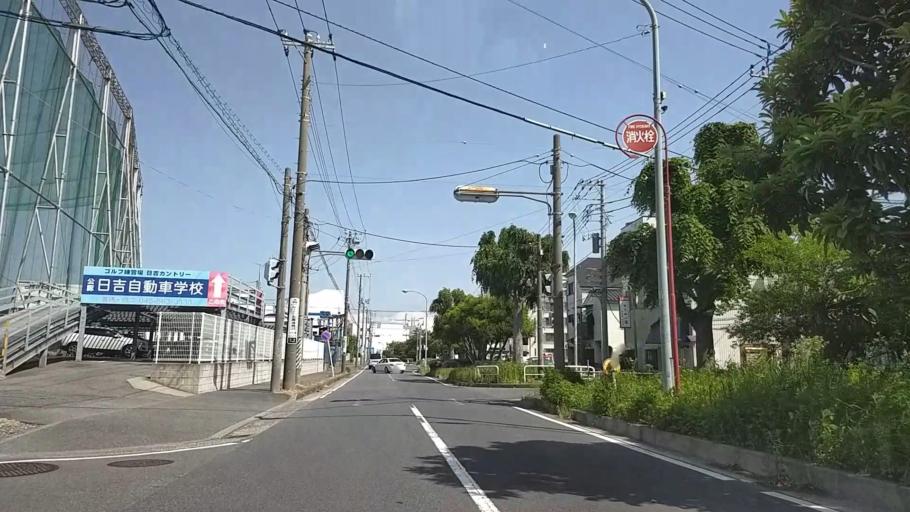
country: JP
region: Kanagawa
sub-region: Kawasaki-shi
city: Kawasaki
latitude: 35.5406
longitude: 139.6501
